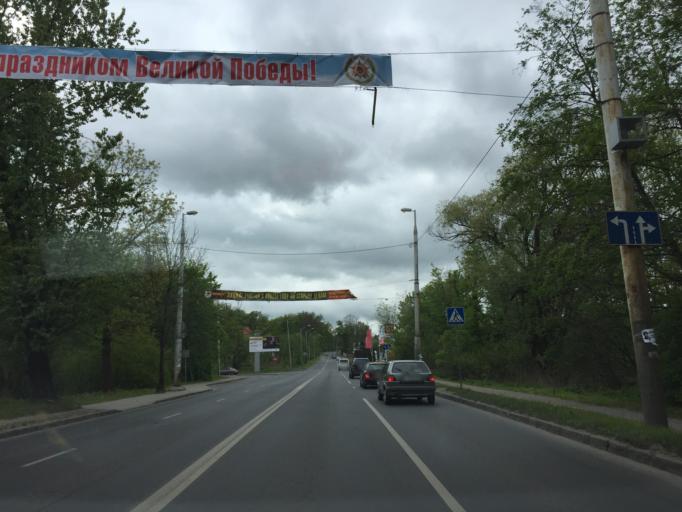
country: RU
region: Kaliningrad
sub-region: Gorod Kaliningrad
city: Kaliningrad
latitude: 54.6862
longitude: 20.4606
